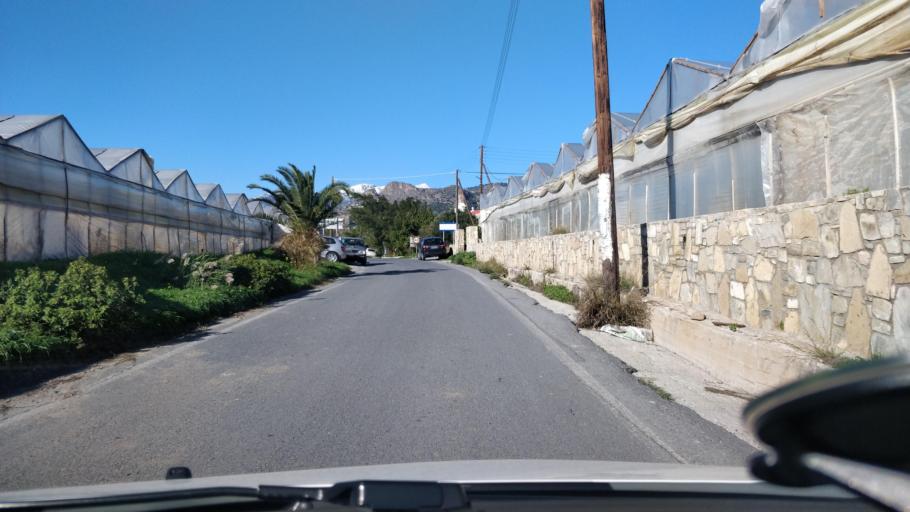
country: GR
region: Crete
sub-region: Nomos Lasithiou
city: Gra Liyia
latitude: 35.0197
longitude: 25.6823
